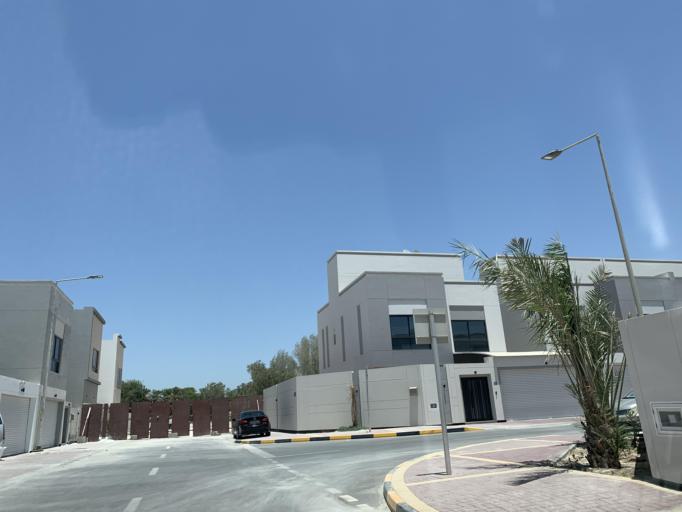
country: BH
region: Manama
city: Jidd Hafs
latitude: 26.2333
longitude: 50.4976
